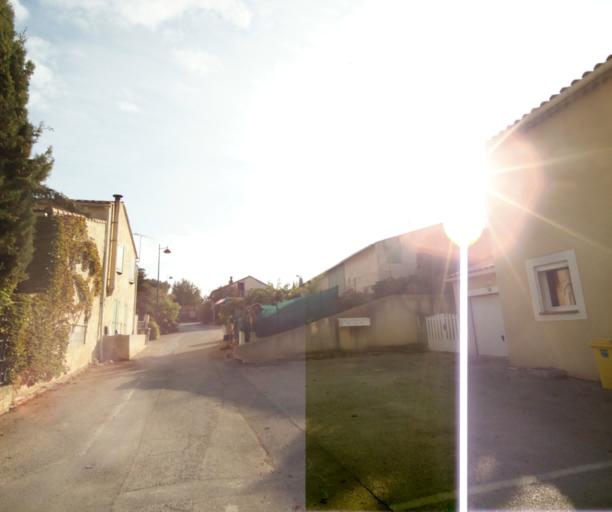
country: FR
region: Provence-Alpes-Cote d'Azur
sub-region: Departement des Bouches-du-Rhone
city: Saint-Victoret
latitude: 43.4141
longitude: 5.2720
